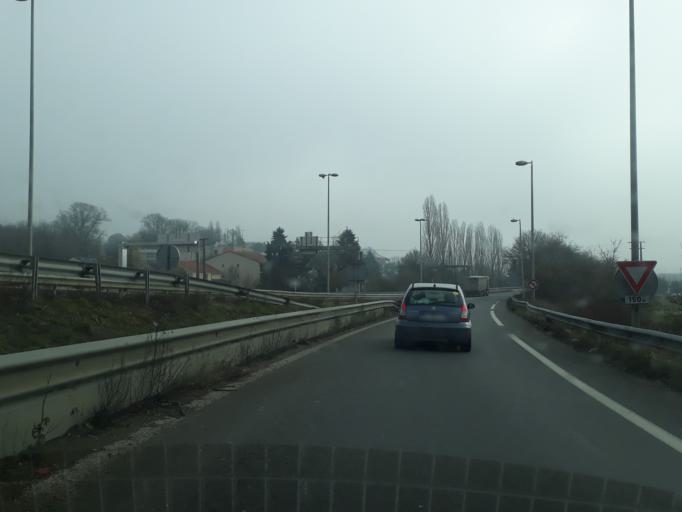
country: FR
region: Lorraine
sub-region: Departement de Meurthe-et-Moselle
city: Bouxieres-aux-Dames
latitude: 48.7506
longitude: 6.1584
